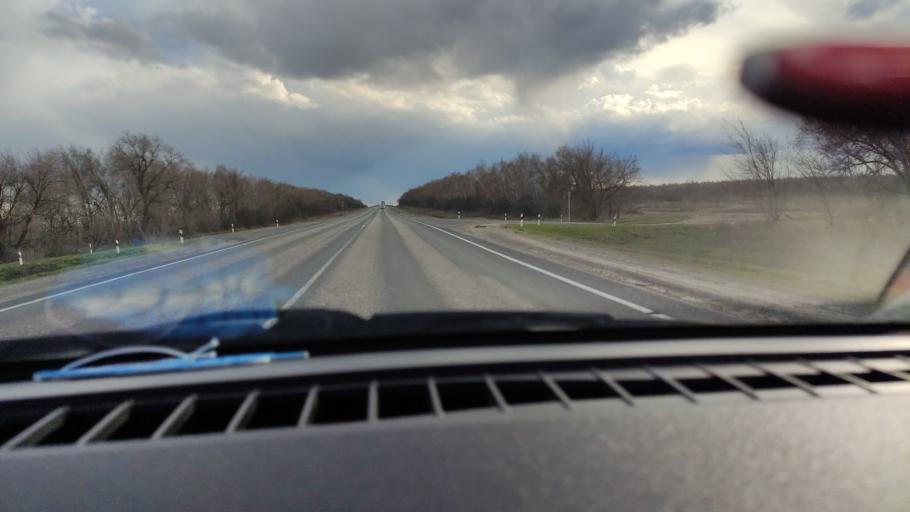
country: RU
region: Saratov
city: Sinodskoye
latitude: 51.9459
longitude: 46.6024
